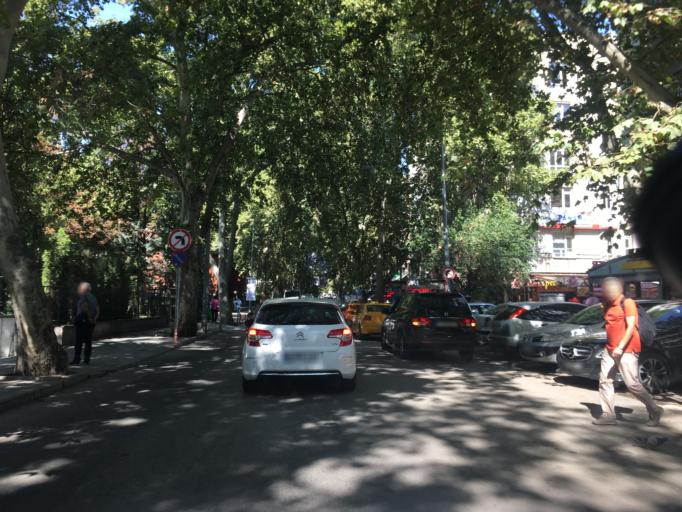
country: TR
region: Ankara
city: Ankara
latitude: 39.9194
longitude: 32.8518
